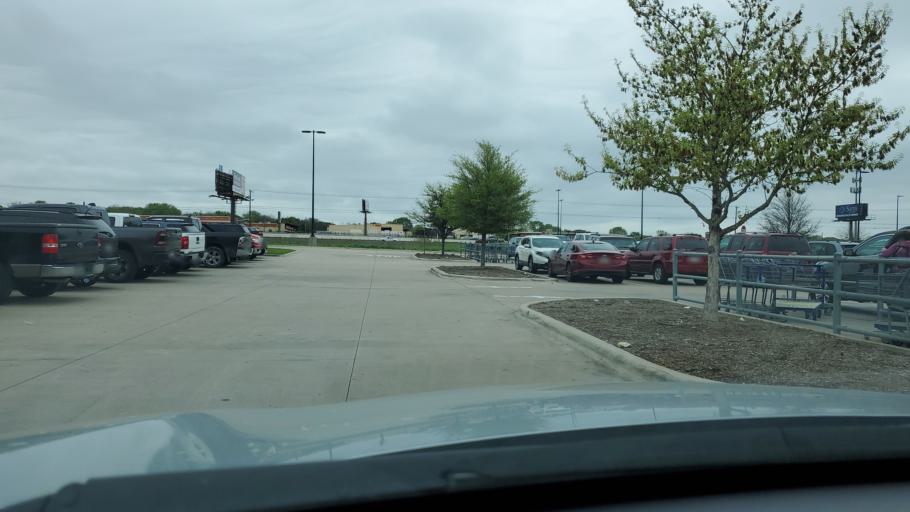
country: US
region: Texas
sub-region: Bell County
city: Harker Heights
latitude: 31.0715
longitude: -97.6804
